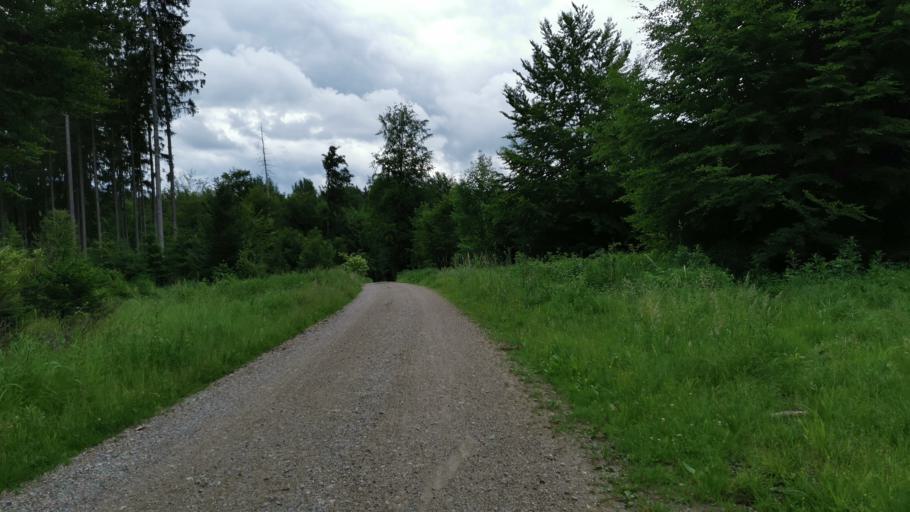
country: DE
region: Bavaria
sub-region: Upper Bavaria
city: Schaftlarn
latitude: 48.0086
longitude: 11.4378
